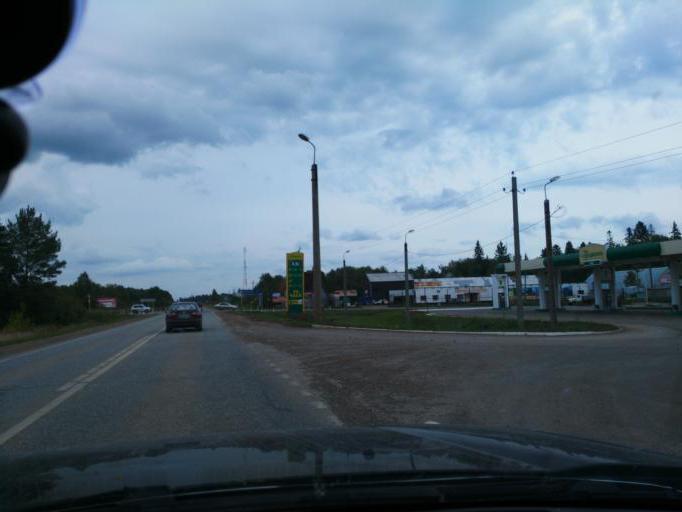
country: RU
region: Perm
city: Chernushka
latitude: 56.5336
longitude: 56.0667
